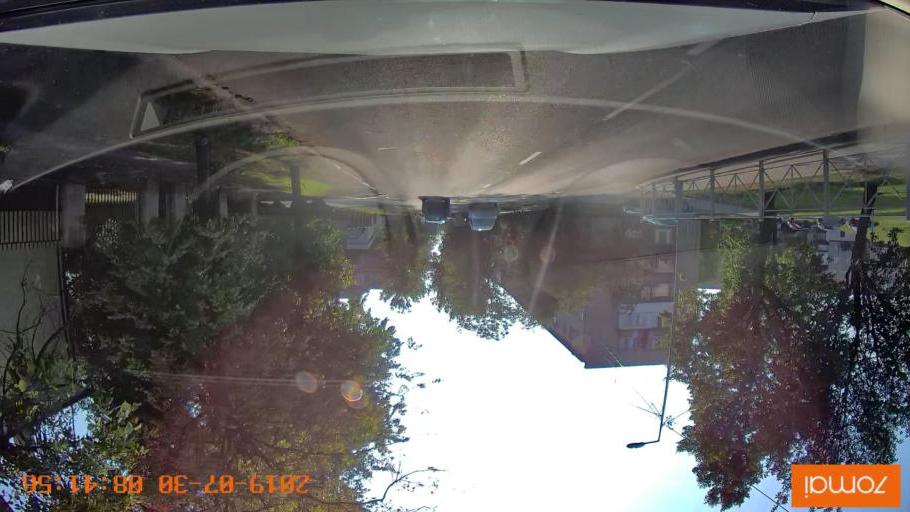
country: RU
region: Kaliningrad
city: Chernyakhovsk
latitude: 54.6300
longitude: 21.8222
